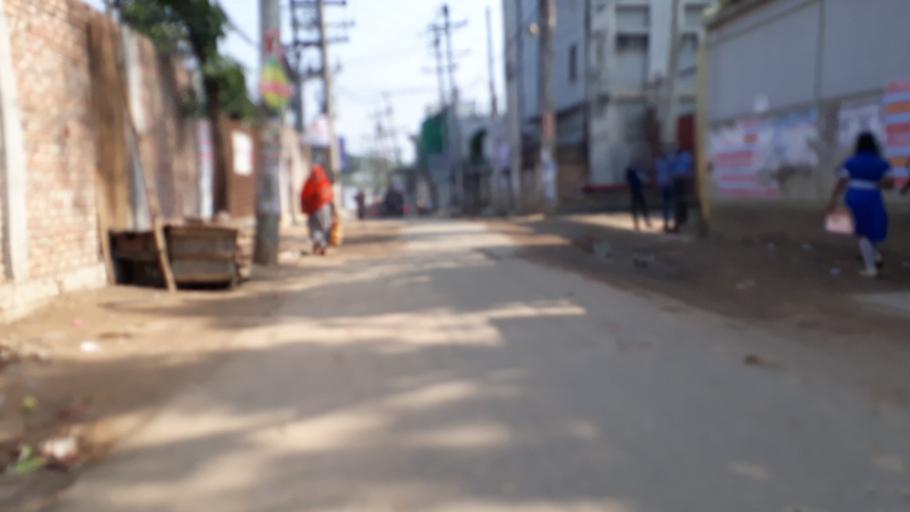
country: BD
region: Dhaka
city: Tungi
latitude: 23.8505
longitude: 90.2853
